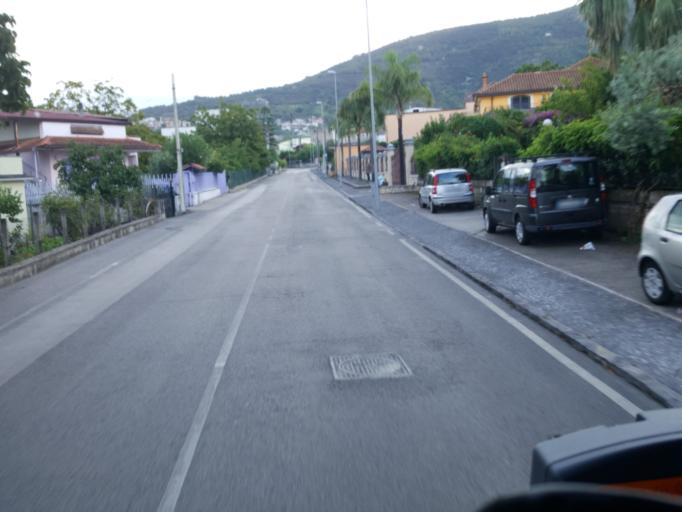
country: IT
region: Campania
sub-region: Provincia di Napoli
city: Carbonara di Nola
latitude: 40.8812
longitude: 14.5731
